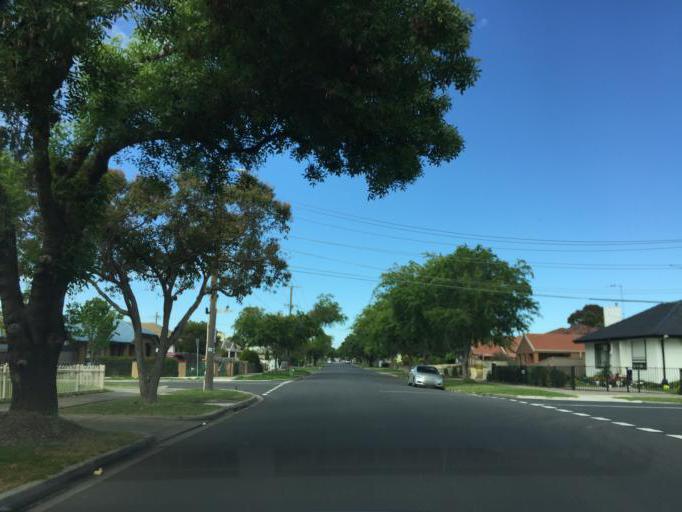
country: AU
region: Victoria
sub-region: Maribyrnong
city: Braybrook
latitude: -37.7872
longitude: 144.8585
